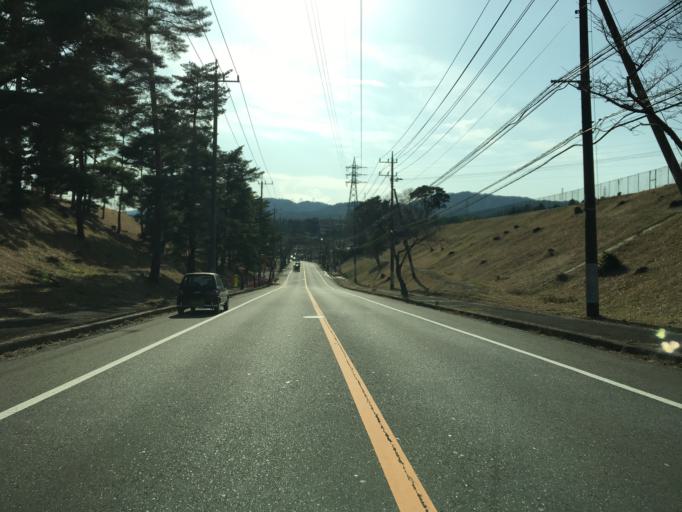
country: JP
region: Ibaraki
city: Takahagi
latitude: 36.7445
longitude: 140.6922
